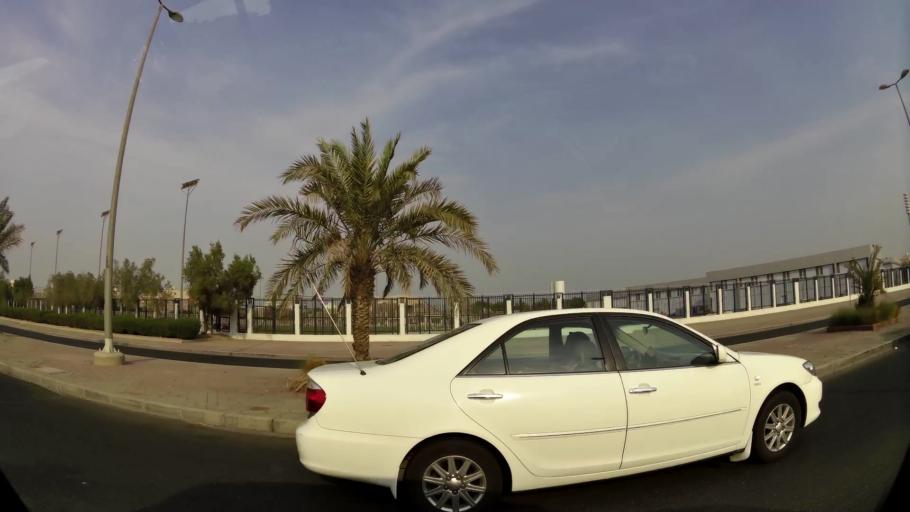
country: KW
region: Mubarak al Kabir
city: Sabah as Salim
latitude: 29.2548
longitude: 48.0548
